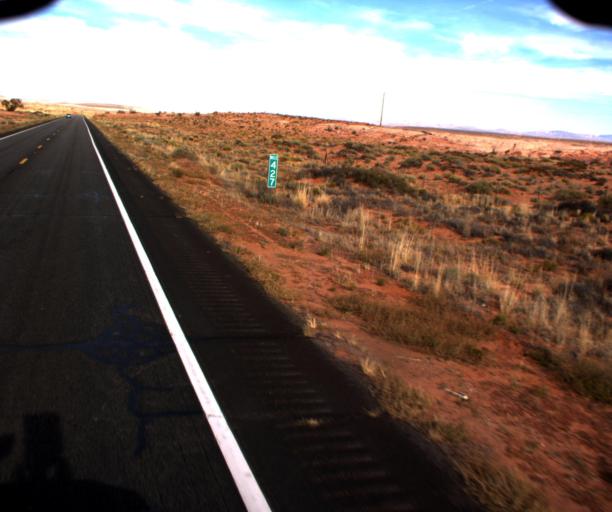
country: US
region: Arizona
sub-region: Navajo County
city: Kayenta
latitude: 36.9343
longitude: -109.7430
